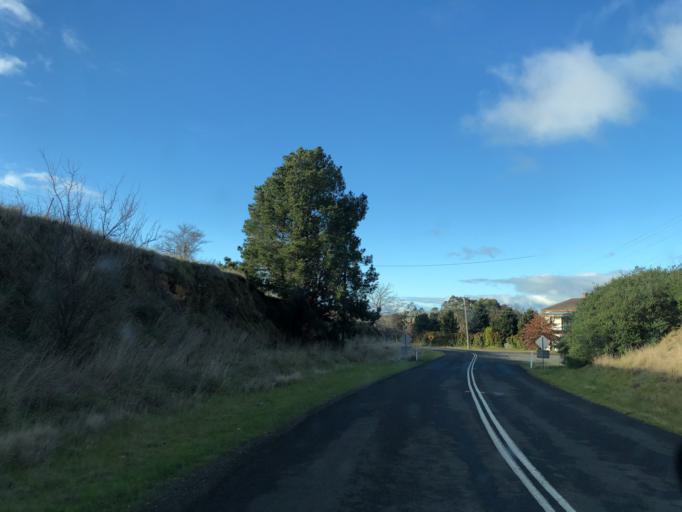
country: AU
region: Victoria
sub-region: Mount Alexander
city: Castlemaine
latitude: -37.1891
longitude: 144.3743
